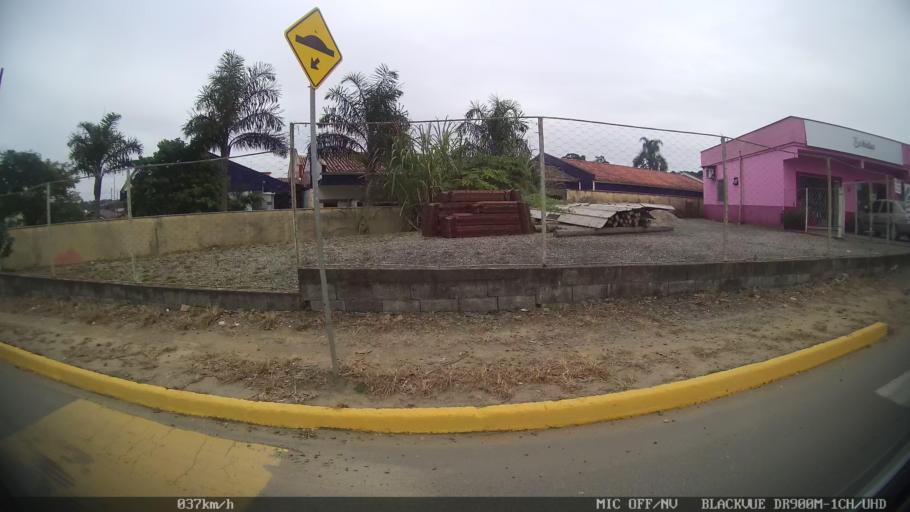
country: BR
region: Santa Catarina
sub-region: Joinville
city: Joinville
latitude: -26.3603
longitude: -48.8076
